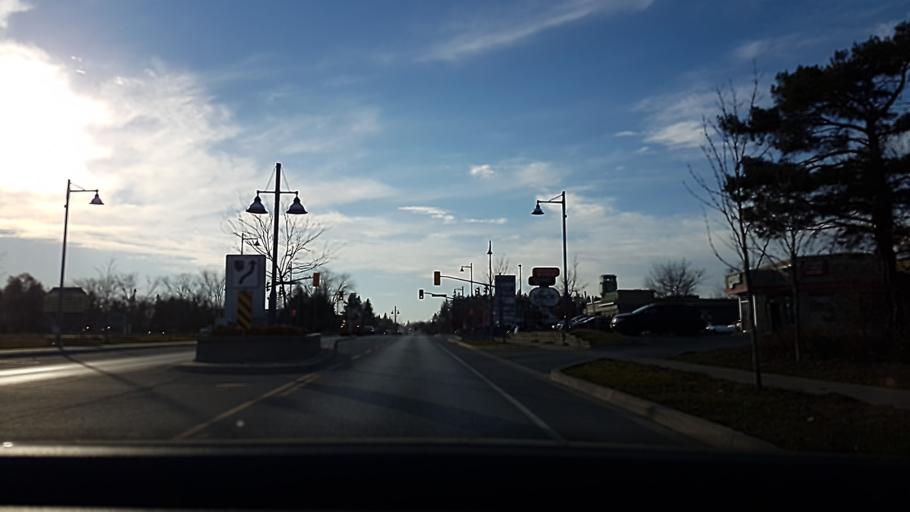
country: CA
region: Ontario
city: Innisfil
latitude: 44.3142
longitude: -79.5516
